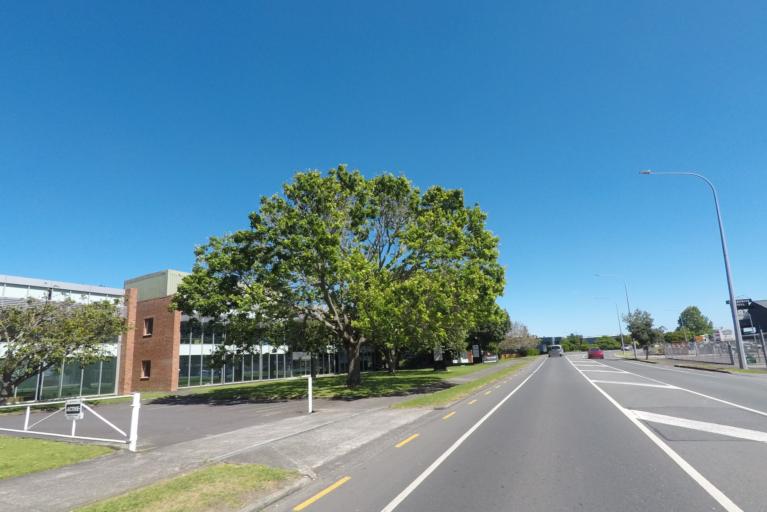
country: NZ
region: Auckland
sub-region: Auckland
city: Rosebank
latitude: -36.8784
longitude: 174.6706
